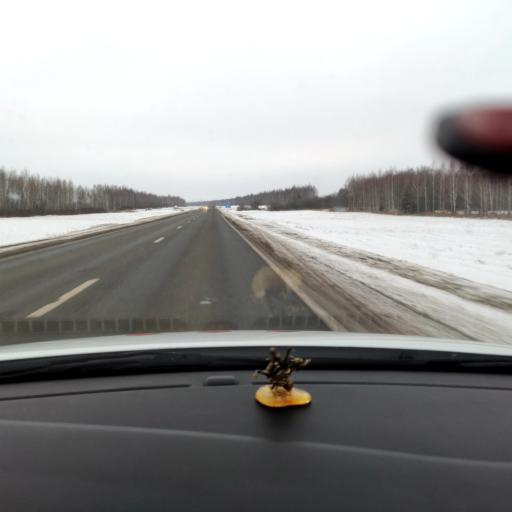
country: RU
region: Tatarstan
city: Stolbishchi
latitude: 55.6226
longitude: 49.2856
